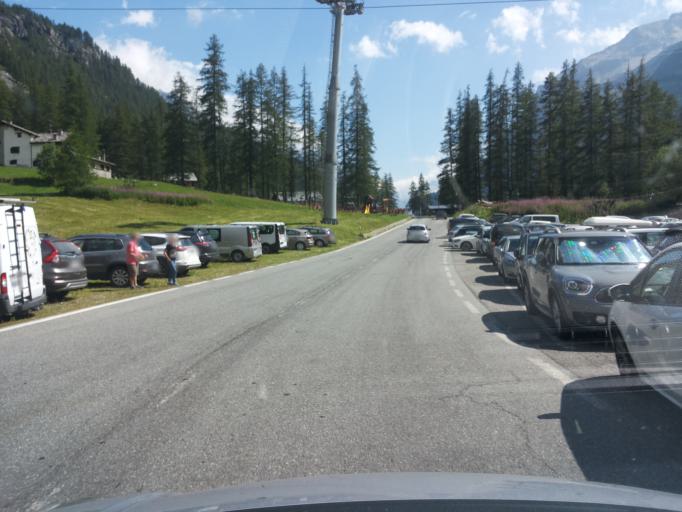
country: IT
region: Aosta Valley
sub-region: Valle d'Aosta
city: Gressoney-La-Trinite
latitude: 45.8583
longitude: 7.8133
